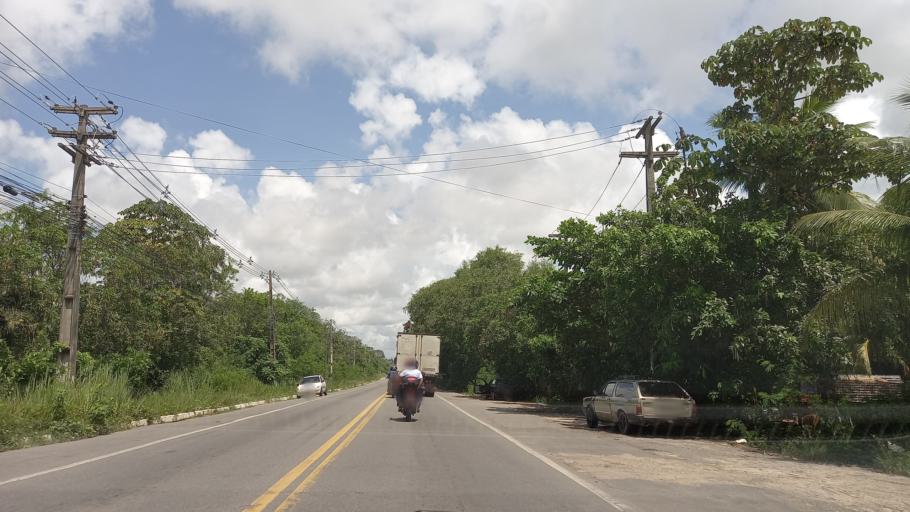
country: BR
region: Pernambuco
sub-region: Jaboatao Dos Guararapes
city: Jaboatao
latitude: -8.2293
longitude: -34.9726
